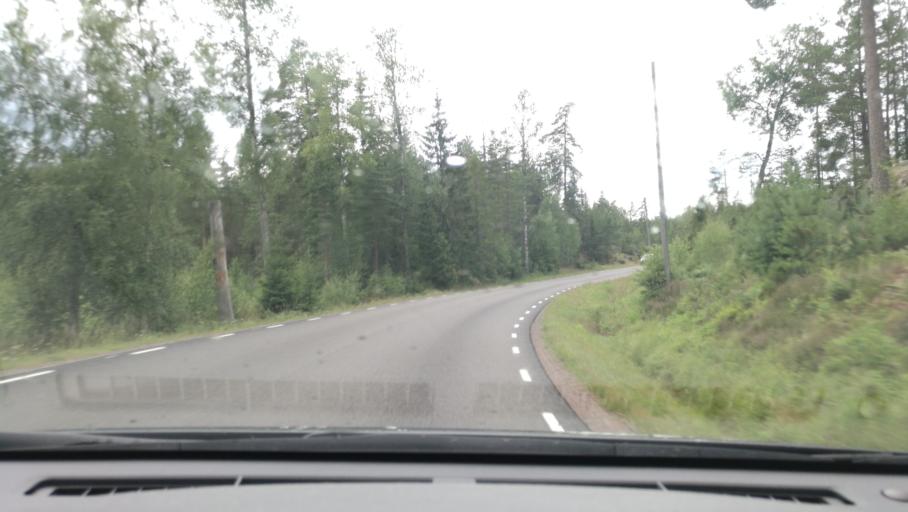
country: SE
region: OEstergoetland
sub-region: Norrkopings Kommun
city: Jursla
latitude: 58.8039
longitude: 16.1285
